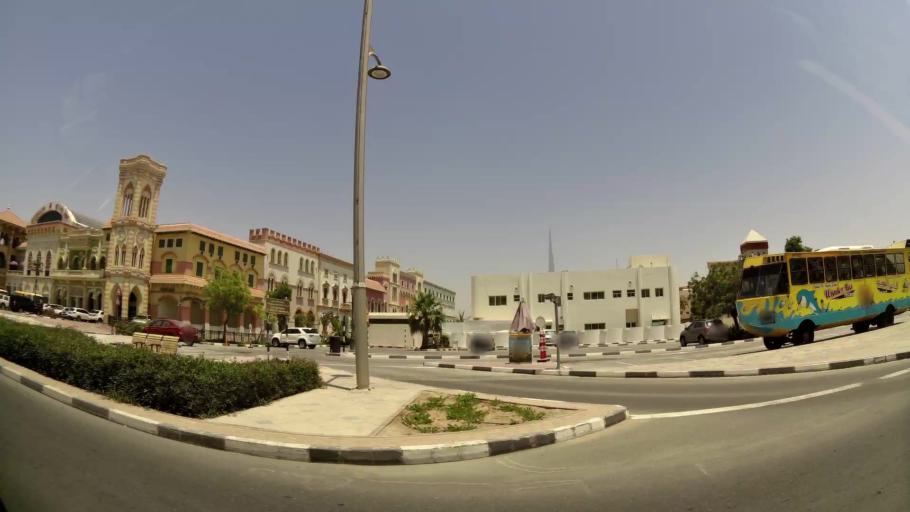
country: AE
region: Dubai
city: Dubai
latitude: 25.2163
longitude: 55.2516
